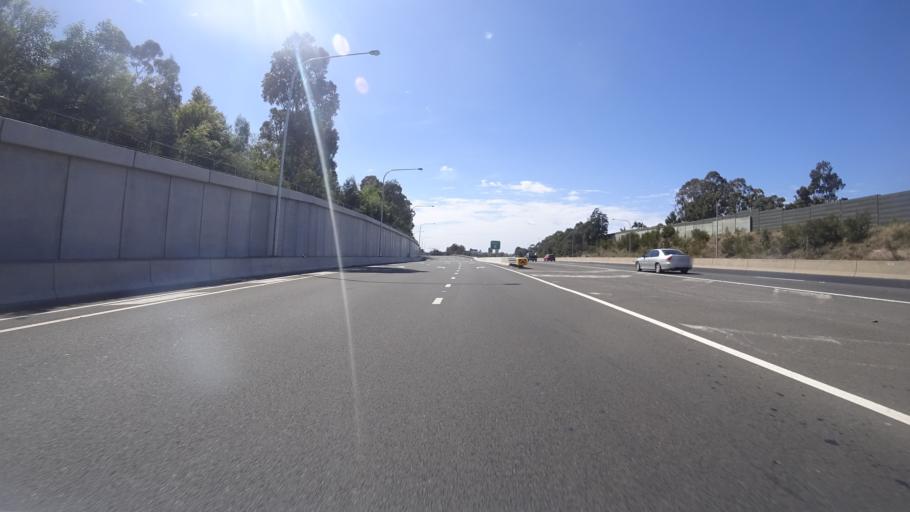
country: AU
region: New South Wales
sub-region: Canterbury
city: Roselands
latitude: -33.9435
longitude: 151.0729
